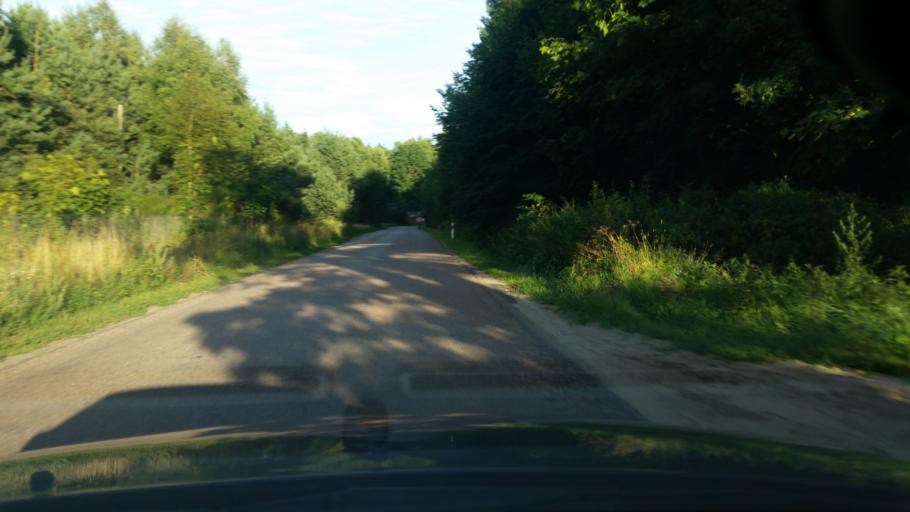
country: PL
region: Pomeranian Voivodeship
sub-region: Powiat wejherowski
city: Choczewo
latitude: 54.7627
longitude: 17.7687
